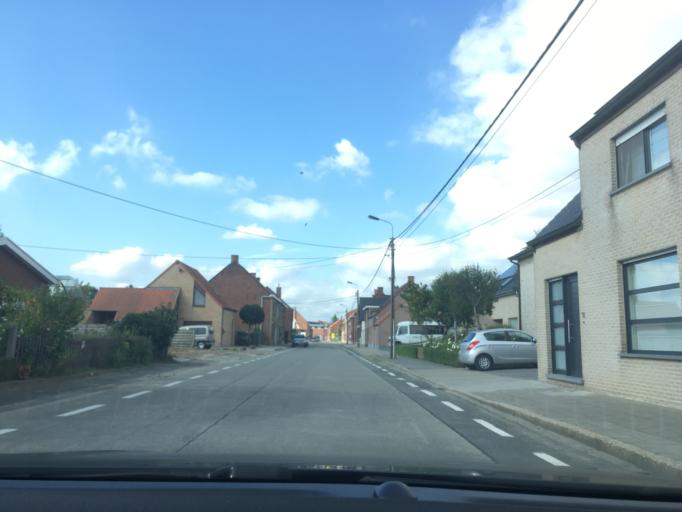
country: BE
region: Flanders
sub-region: Provincie West-Vlaanderen
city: Moorslede
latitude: 50.9350
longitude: 3.0625
